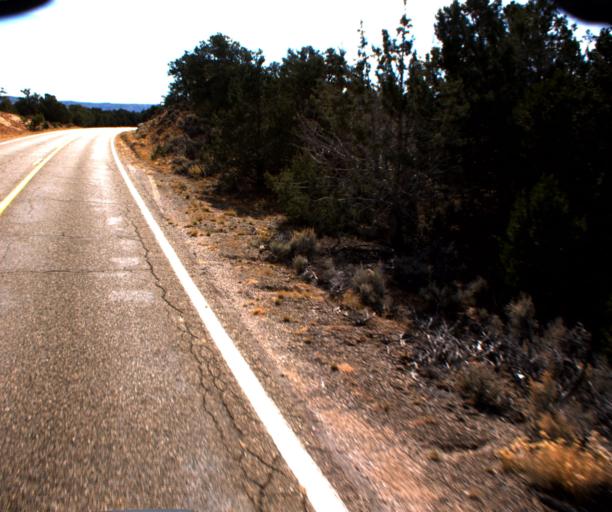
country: US
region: Arizona
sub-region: Navajo County
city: Kayenta
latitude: 36.6417
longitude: -110.5131
